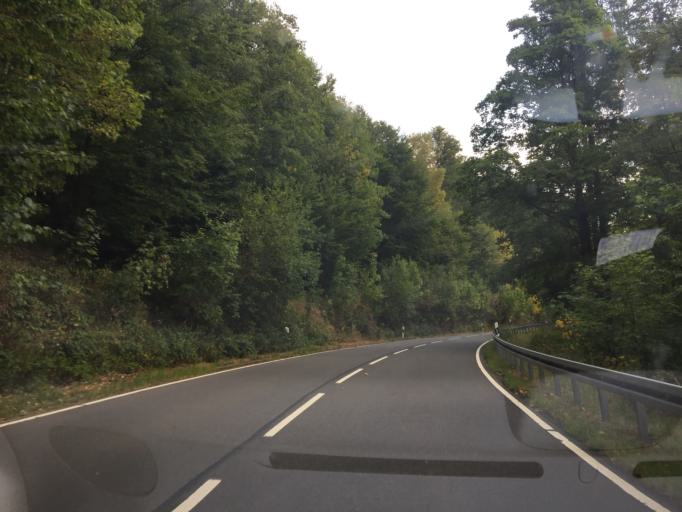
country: DE
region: Lower Saxony
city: Zorge
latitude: 51.6524
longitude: 10.6529
